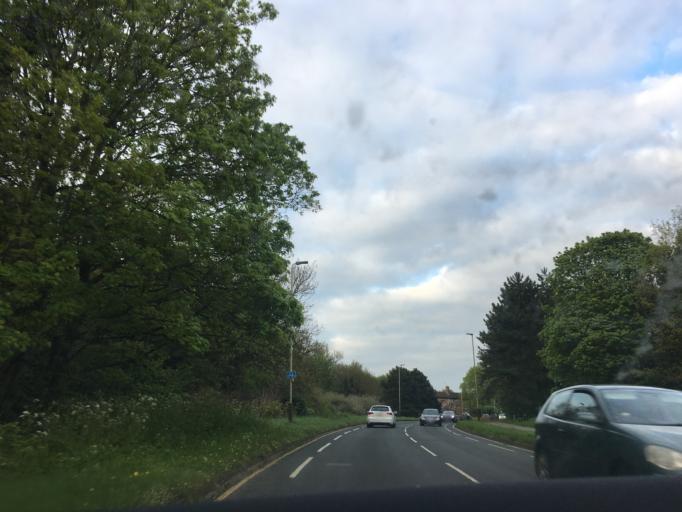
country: GB
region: England
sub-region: Leicestershire
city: Oadby
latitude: 52.6271
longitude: -1.0810
